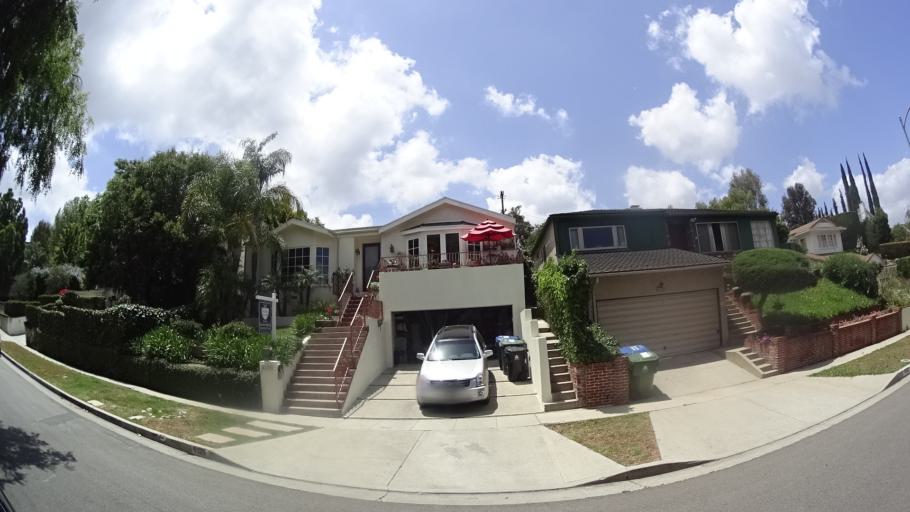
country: US
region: California
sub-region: Los Angeles County
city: Sherman Oaks
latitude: 34.1457
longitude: -118.4323
